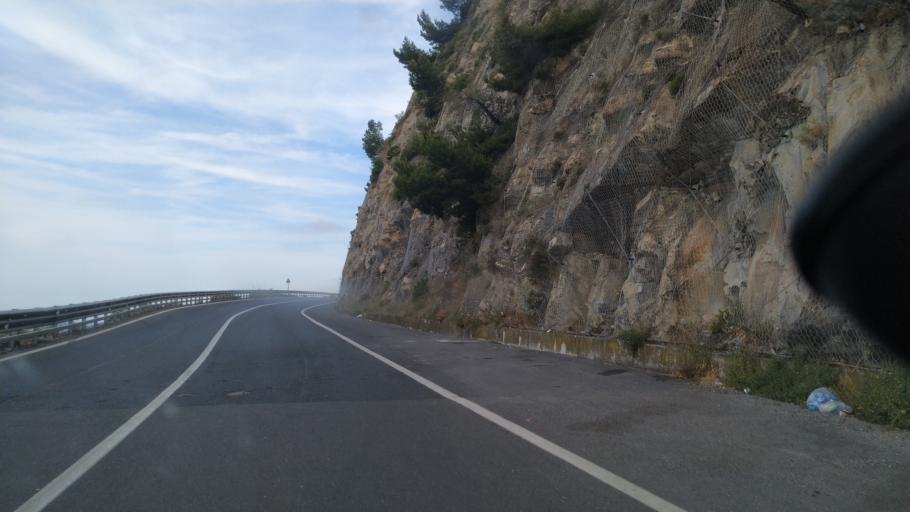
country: IT
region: Liguria
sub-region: Provincia di Savona
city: Marina di Andora
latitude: 43.9624
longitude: 8.1676
